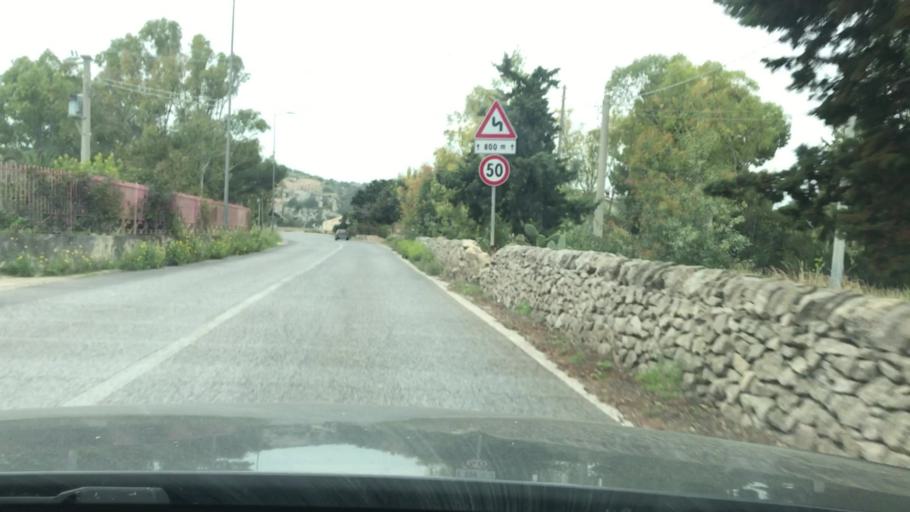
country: IT
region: Sicily
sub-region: Ragusa
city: Scicli
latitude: 36.7969
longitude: 14.7108
